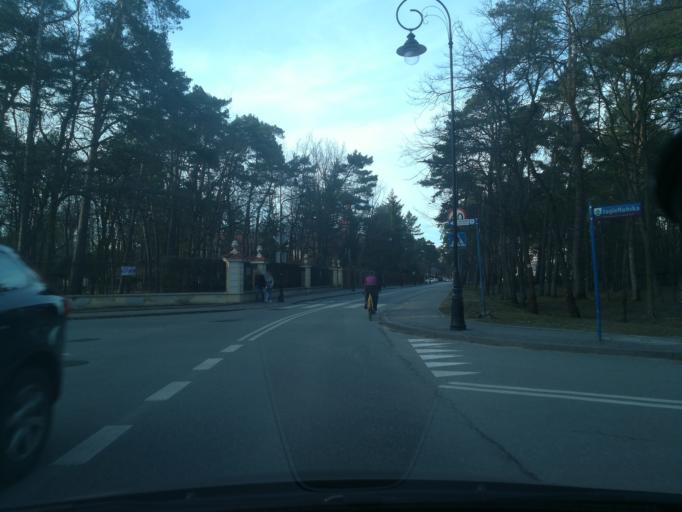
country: PL
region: Masovian Voivodeship
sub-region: Powiat piaseczynski
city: Konstancin-Jeziorna
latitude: 52.0809
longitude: 21.1190
